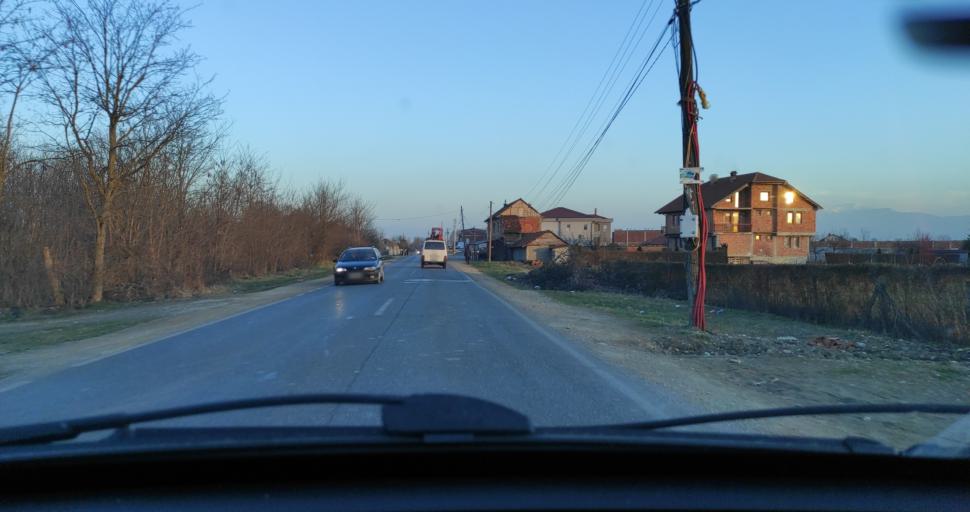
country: XK
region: Gjakova
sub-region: Komuna e Decanit
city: Gllogjan
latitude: 42.4357
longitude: 20.3740
